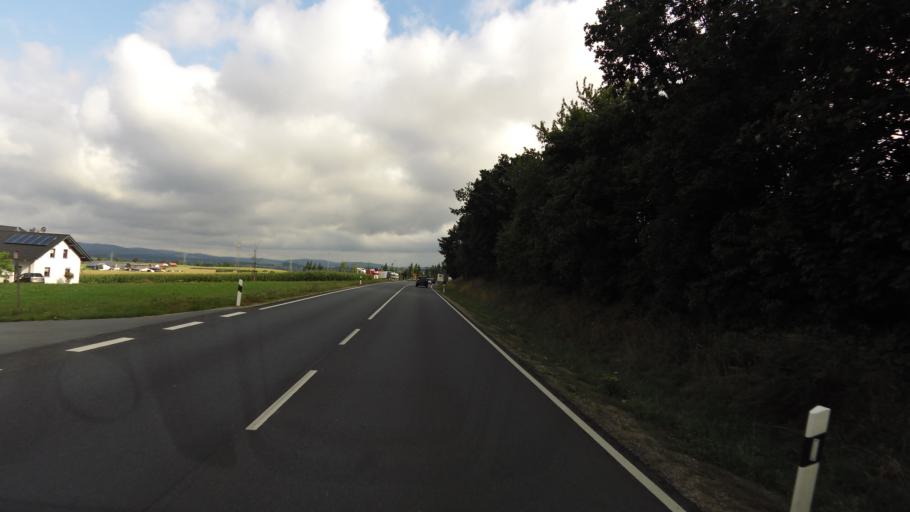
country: DE
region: Bavaria
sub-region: Upper Palatinate
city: Cham
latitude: 49.1937
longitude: 12.6562
